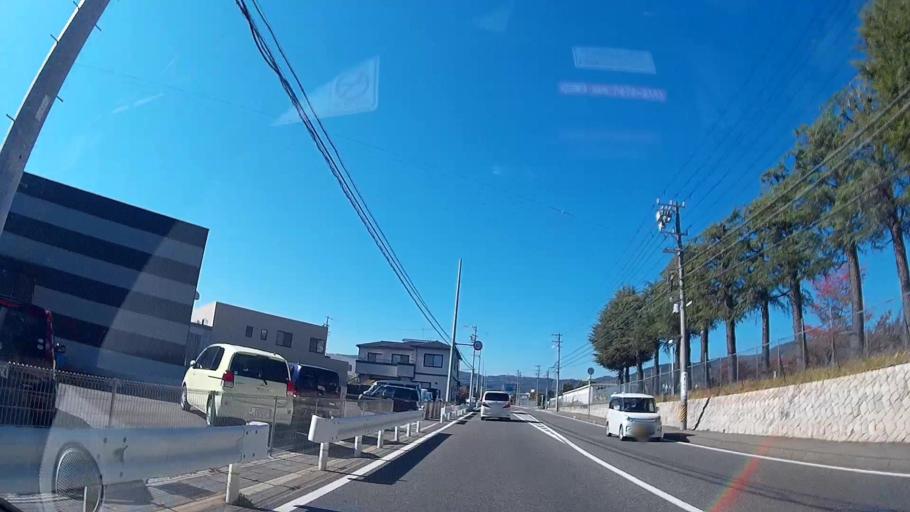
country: JP
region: Nagano
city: Okaya
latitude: 36.0787
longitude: 138.0637
